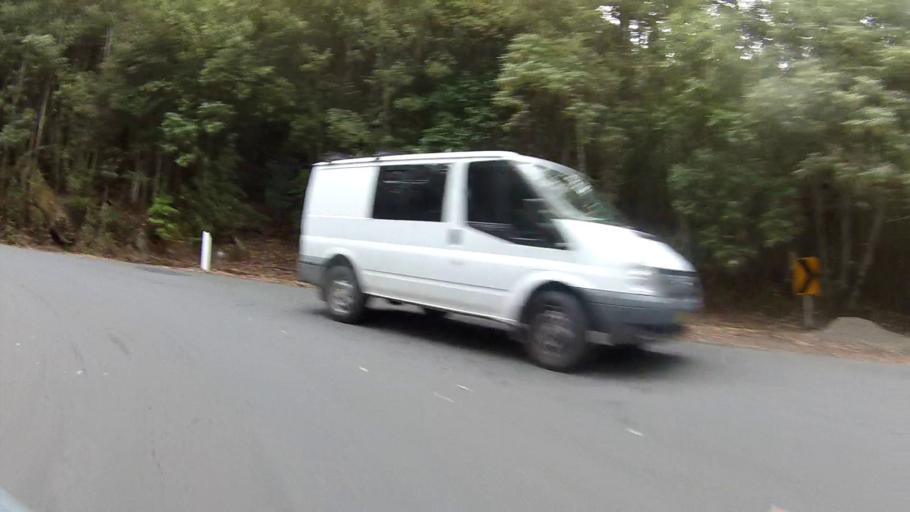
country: AU
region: Tasmania
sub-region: Glenorchy
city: West Moonah
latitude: -42.9085
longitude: 147.2480
